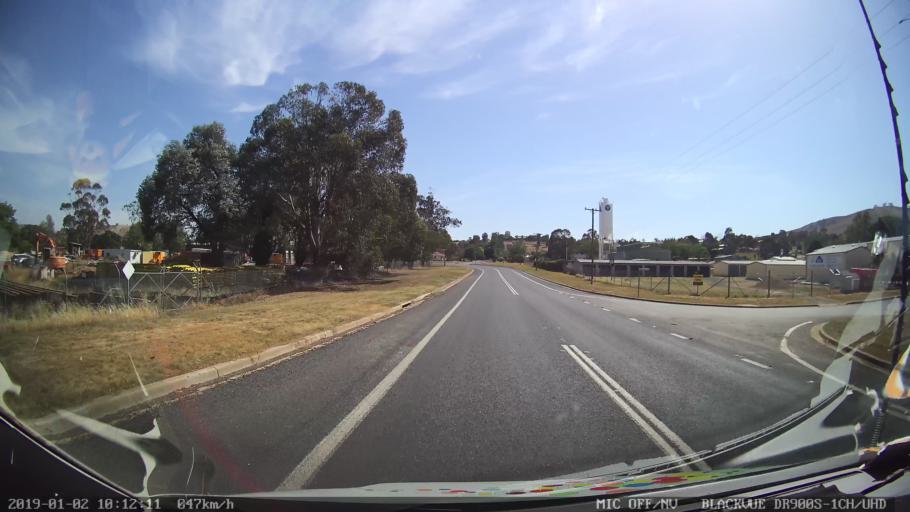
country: AU
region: New South Wales
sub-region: Gundagai
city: Gundagai
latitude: -35.0863
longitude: 148.0944
